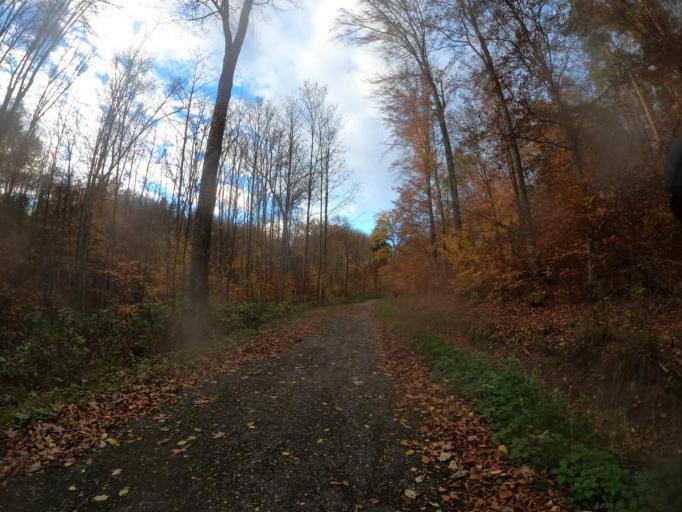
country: DE
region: Baden-Wuerttemberg
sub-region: Regierungsbezirk Stuttgart
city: Sindelfingen
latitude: 48.7146
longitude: 9.0326
